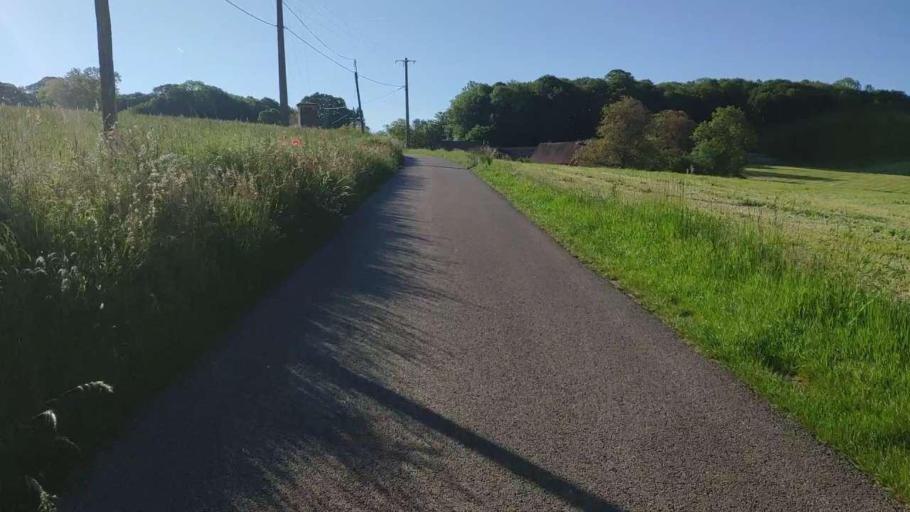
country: FR
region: Franche-Comte
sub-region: Departement du Jura
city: Perrigny
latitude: 46.7170
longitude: 5.6170
